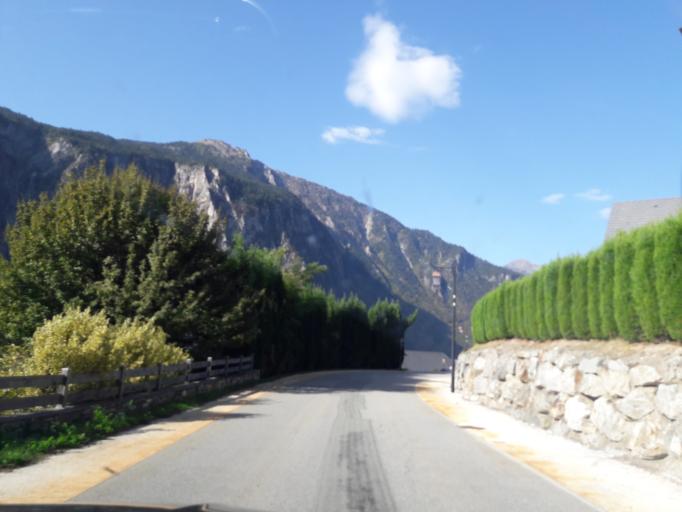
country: FR
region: Rhone-Alpes
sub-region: Departement de la Savoie
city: Saint-Jean-de-Maurienne
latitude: 45.3137
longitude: 6.3506
